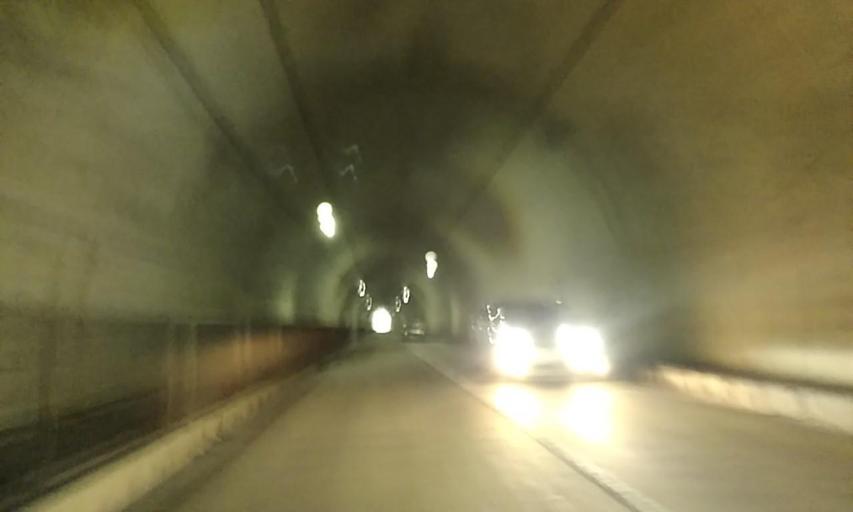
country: JP
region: Mie
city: Ise
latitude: 34.2697
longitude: 136.4894
